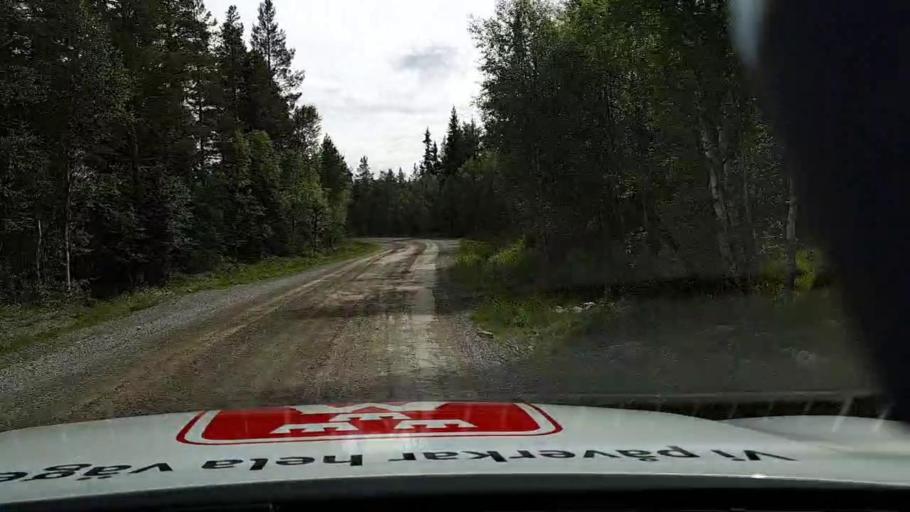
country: SE
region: Jaemtland
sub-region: Are Kommun
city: Jarpen
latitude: 62.4983
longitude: 13.5014
